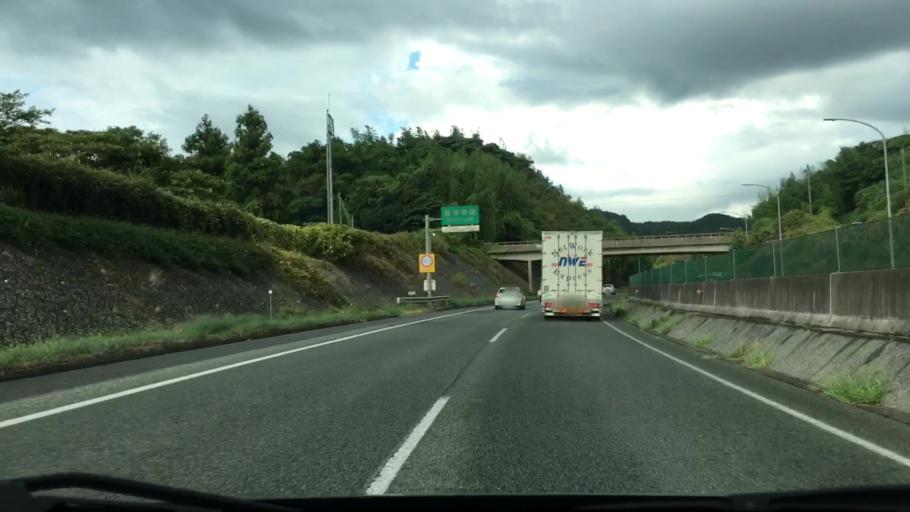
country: JP
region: Fukuoka
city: Nishifukuma
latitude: 33.7505
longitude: 130.5373
